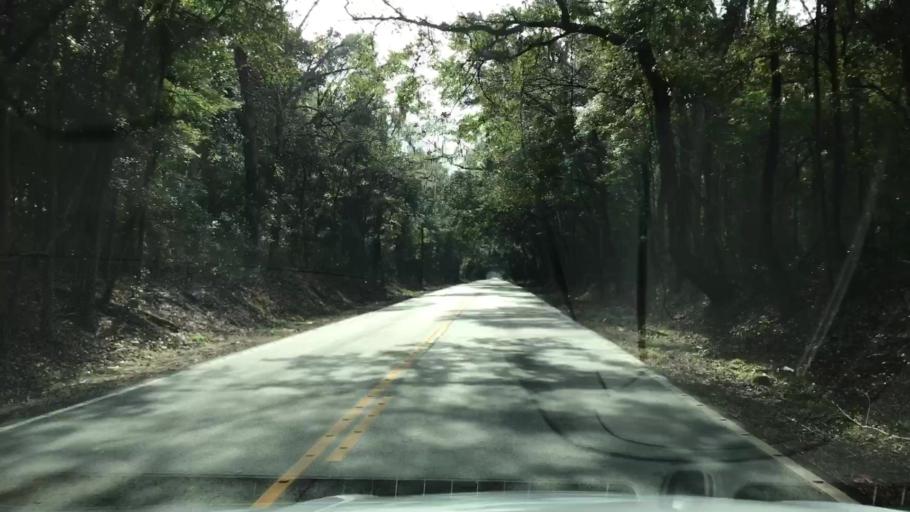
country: US
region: South Carolina
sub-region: Charleston County
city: Folly Beach
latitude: 32.7123
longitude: -80.0185
